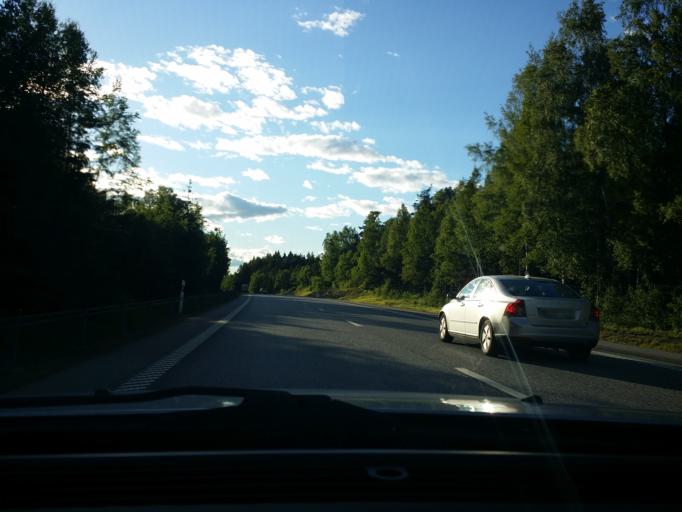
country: SE
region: Stockholm
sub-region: Upplands-Bro Kommun
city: Bro
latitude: 59.5518
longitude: 17.5917
